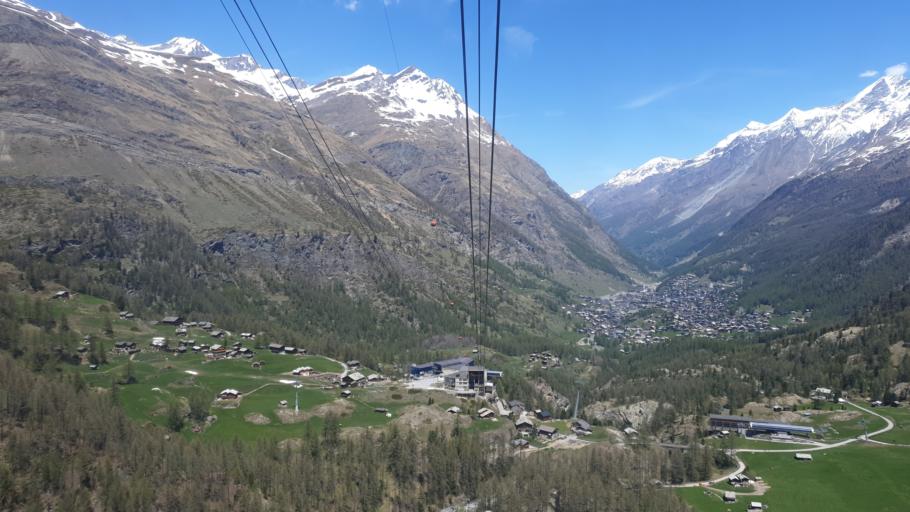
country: CH
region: Valais
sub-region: Visp District
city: Zermatt
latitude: 45.9956
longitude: 7.7304
